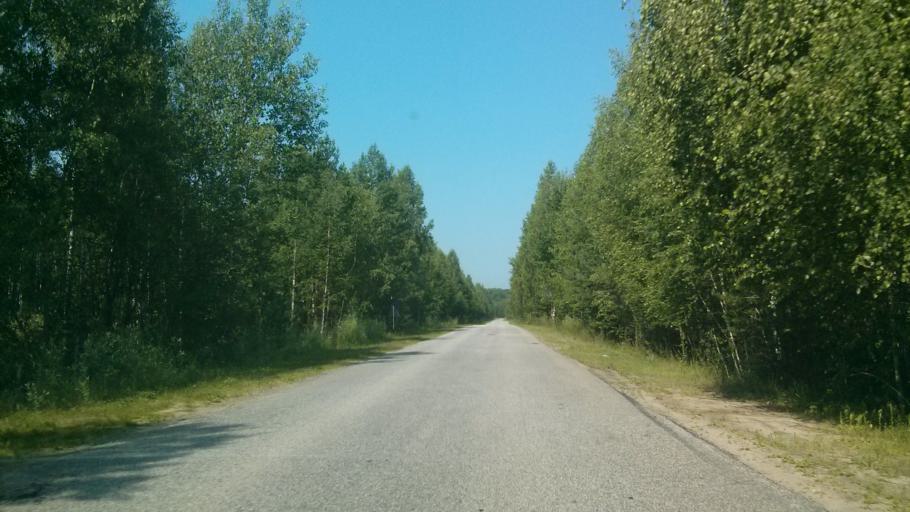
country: RU
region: Vladimir
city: Murom
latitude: 55.5058
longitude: 42.0028
